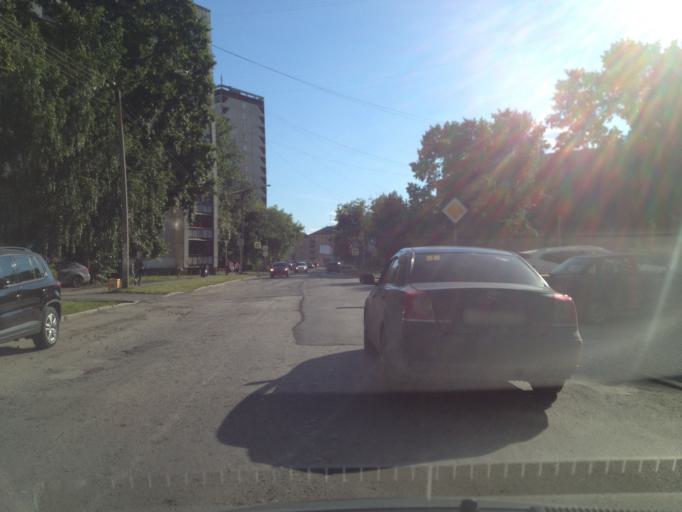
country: RU
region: Sverdlovsk
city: Yekaterinburg
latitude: 56.9061
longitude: 60.6169
